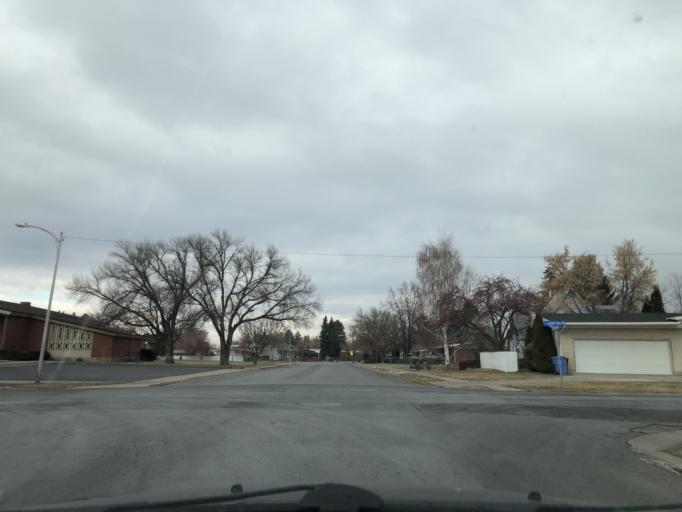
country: US
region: Utah
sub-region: Cache County
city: Logan
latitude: 41.7425
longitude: -111.8373
